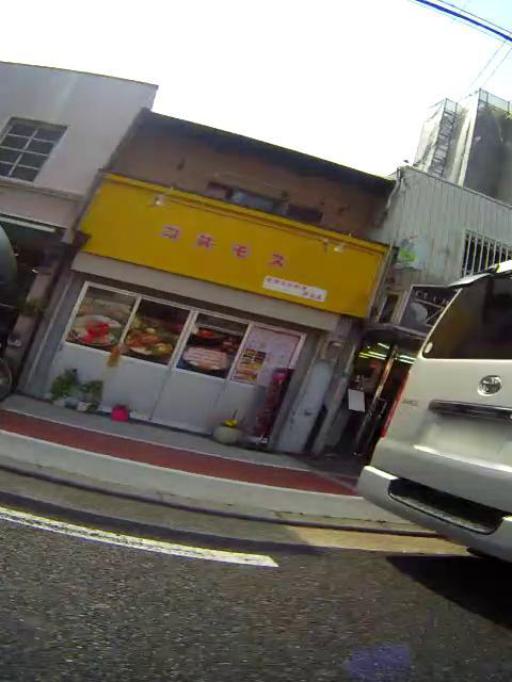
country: JP
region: Osaka
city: Osaka-shi
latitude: 34.6841
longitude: 135.5450
